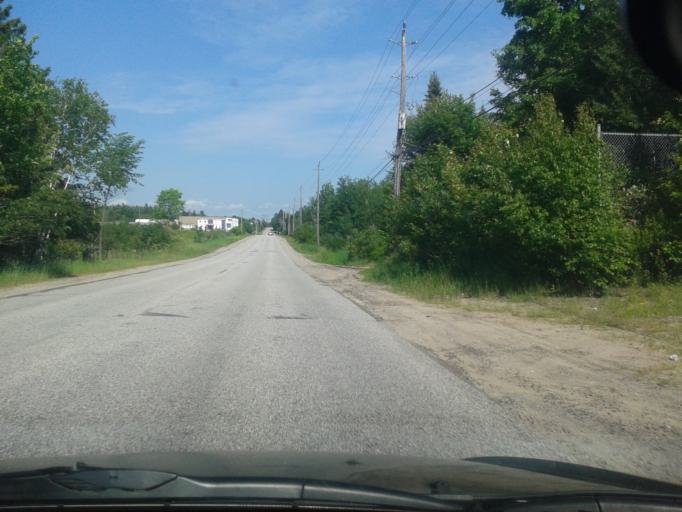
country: CA
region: Ontario
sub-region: Nipissing District
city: North Bay
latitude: 46.3471
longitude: -79.4763
